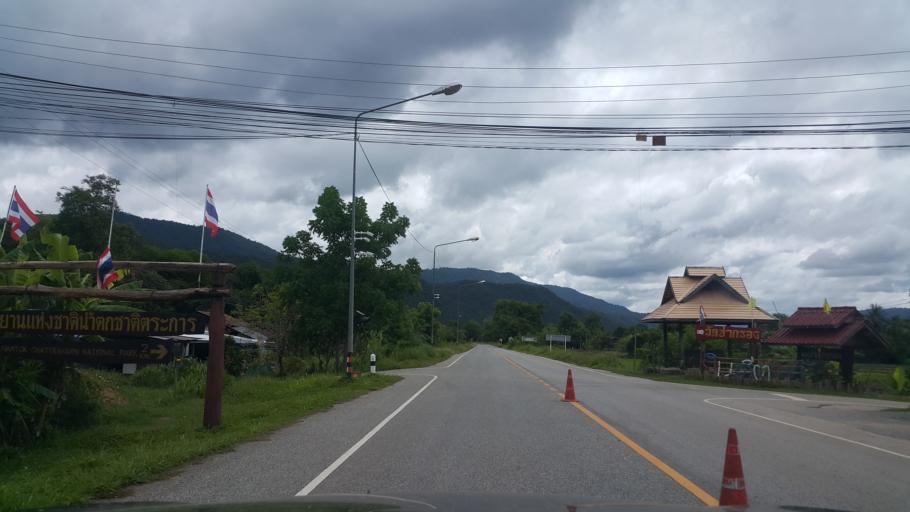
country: TH
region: Phitsanulok
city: Chat Trakan
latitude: 17.3043
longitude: 100.6677
